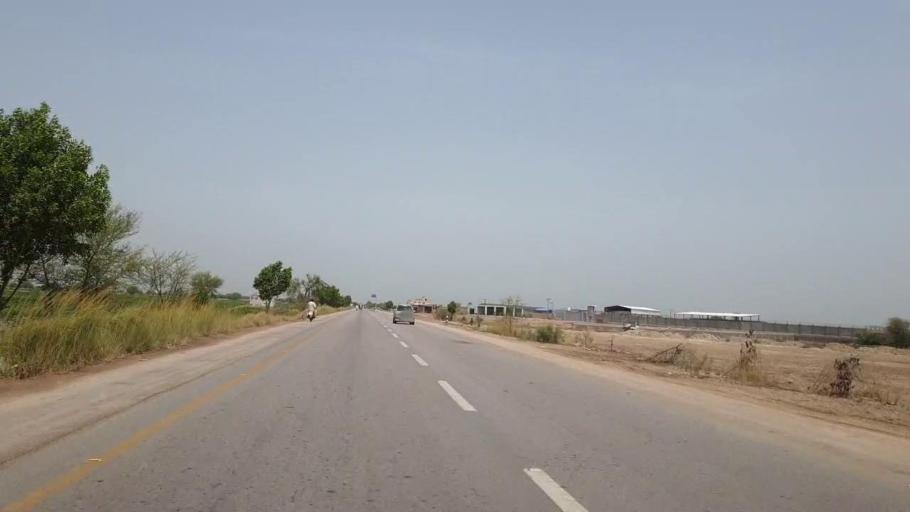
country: PK
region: Sindh
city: Nawabshah
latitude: 26.2291
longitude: 68.4875
